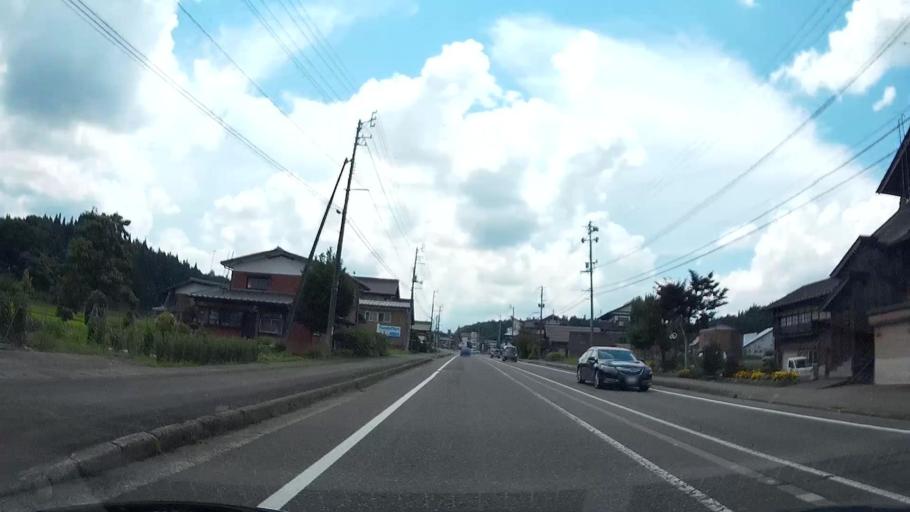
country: JP
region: Niigata
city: Tokamachi
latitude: 37.0393
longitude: 138.6761
